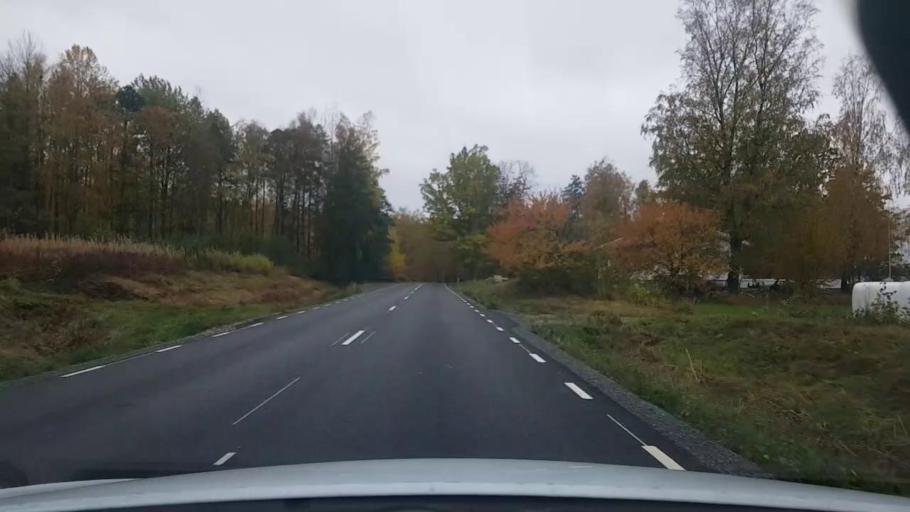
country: SE
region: Vaestra Goetaland
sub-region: Karlsborgs Kommun
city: Karlsborg
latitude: 58.7646
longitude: 14.5253
